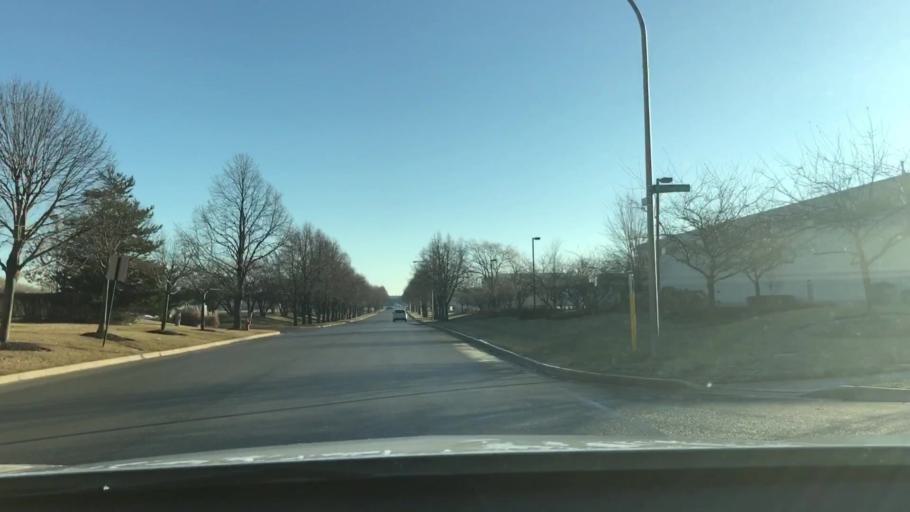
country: US
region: Illinois
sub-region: Kane County
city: Gilberts
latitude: 42.0753
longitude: -88.3444
